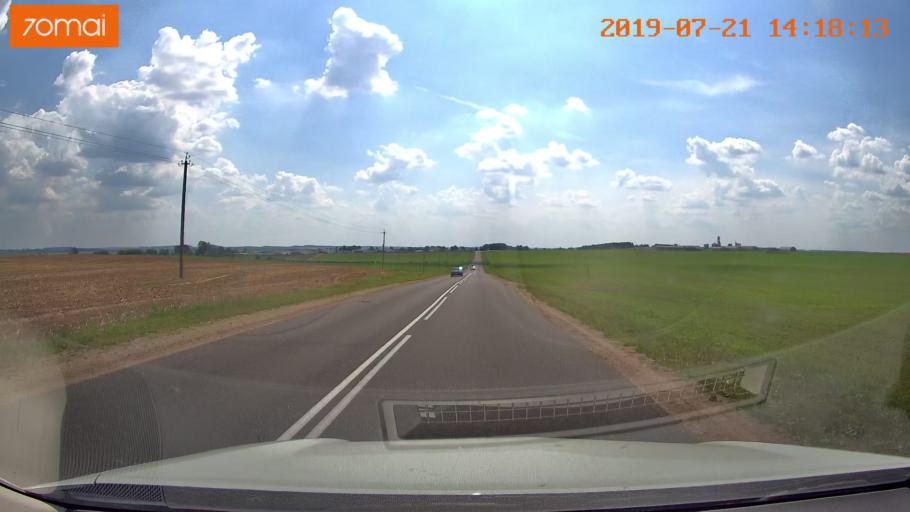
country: BY
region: Grodnenskaya
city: Karelichy
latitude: 53.5990
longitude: 26.1808
